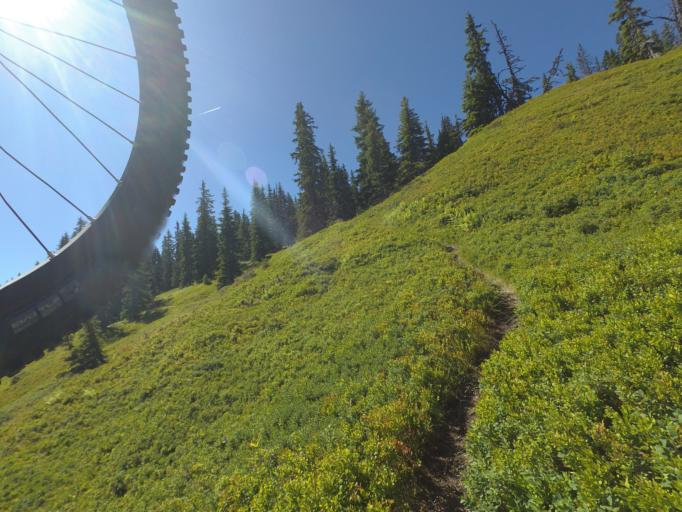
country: AT
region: Salzburg
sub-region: Politischer Bezirk Sankt Johann im Pongau
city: Goldegg
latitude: 47.3540
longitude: 13.0744
